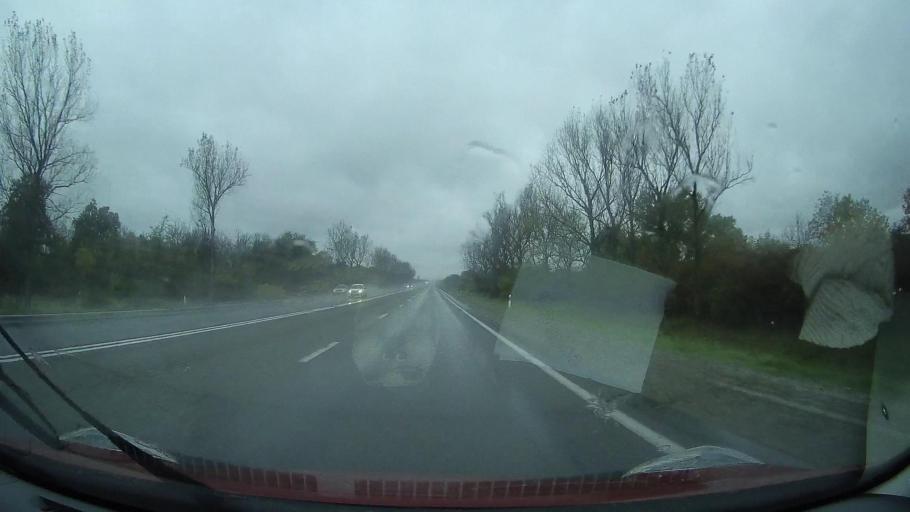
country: RU
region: Stavropol'skiy
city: Nevinnomyssk
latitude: 44.6299
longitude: 42.0325
